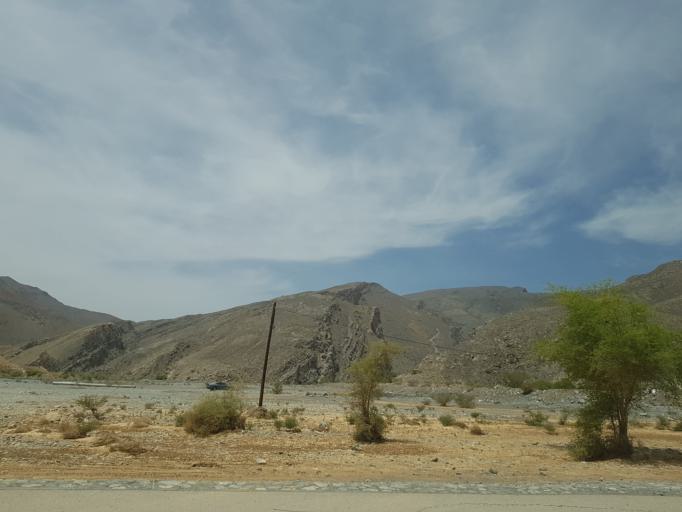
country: OM
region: Muhafazat ad Dakhiliyah
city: Izki
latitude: 22.9497
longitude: 57.6717
